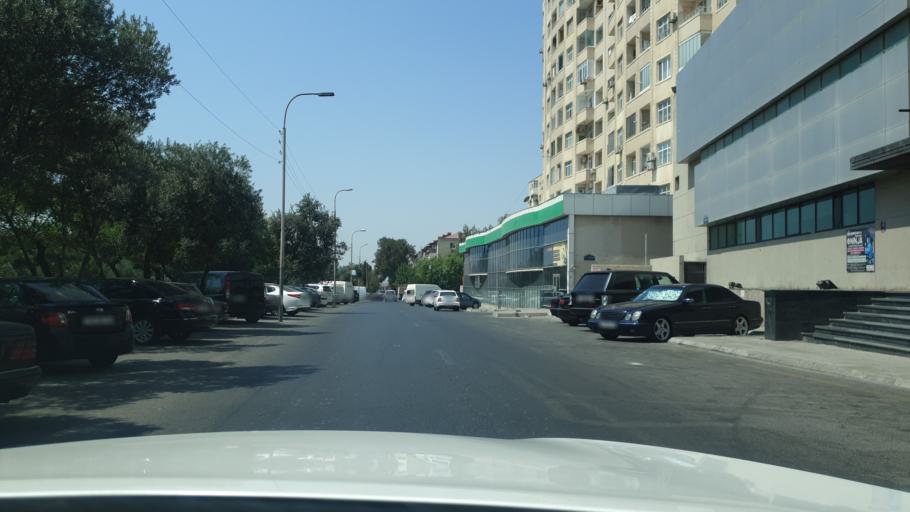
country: AZ
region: Baki
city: Bakixanov
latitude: 40.4136
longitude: 49.9507
